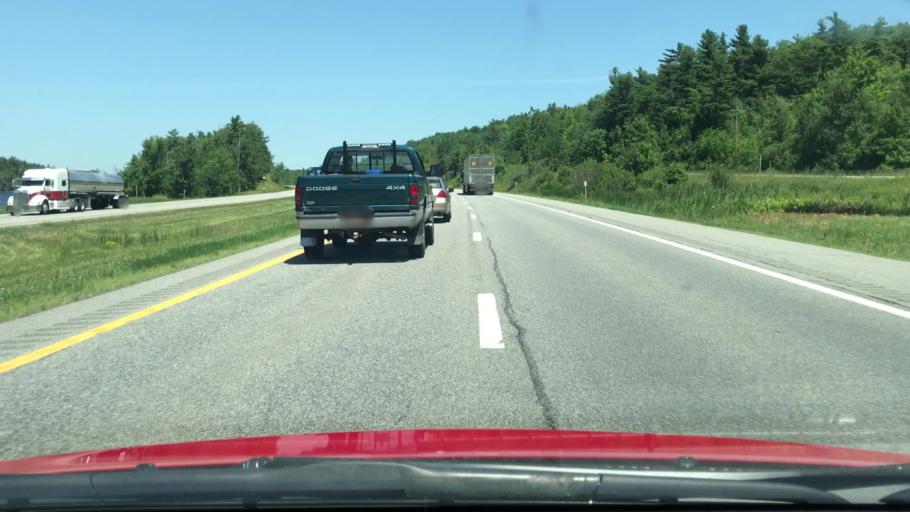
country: US
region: New York
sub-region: Essex County
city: Keeseville
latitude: 44.4256
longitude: -73.4923
